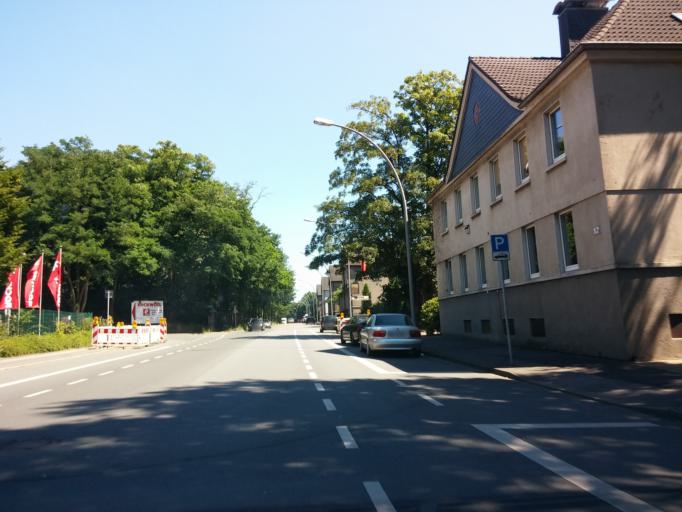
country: DE
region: North Rhine-Westphalia
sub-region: Regierungsbezirk Munster
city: Gladbeck
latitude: 51.5703
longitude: 6.9667
